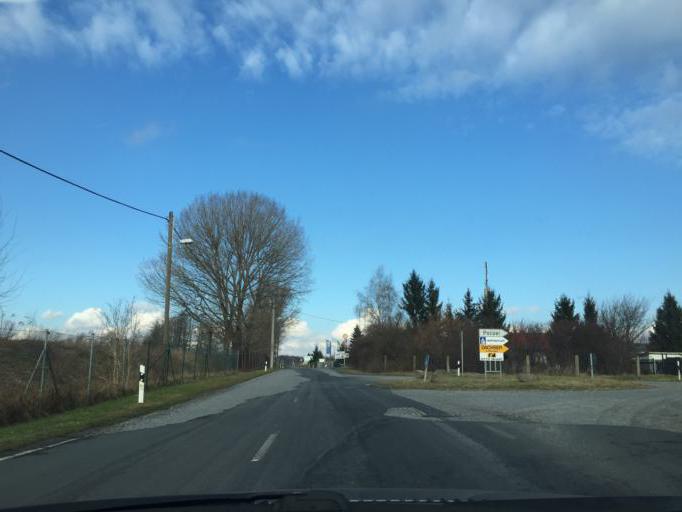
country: DE
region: Saxony
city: Radeburg
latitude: 51.2198
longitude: 13.7254
